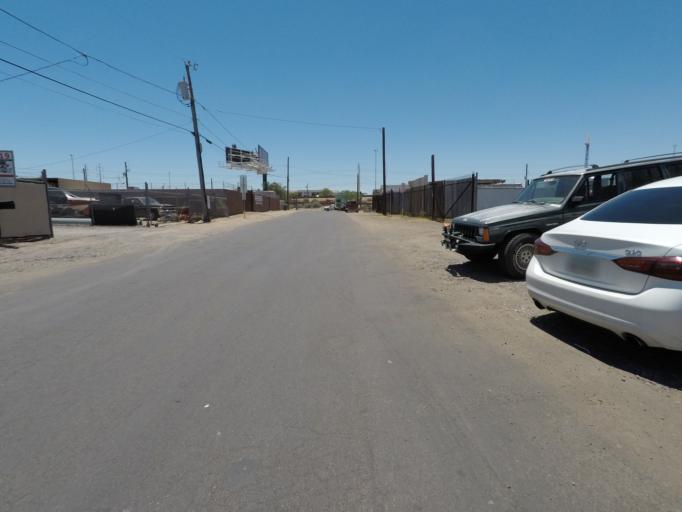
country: US
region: Arizona
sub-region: Maricopa County
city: Tempe
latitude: 33.4375
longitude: -111.9237
